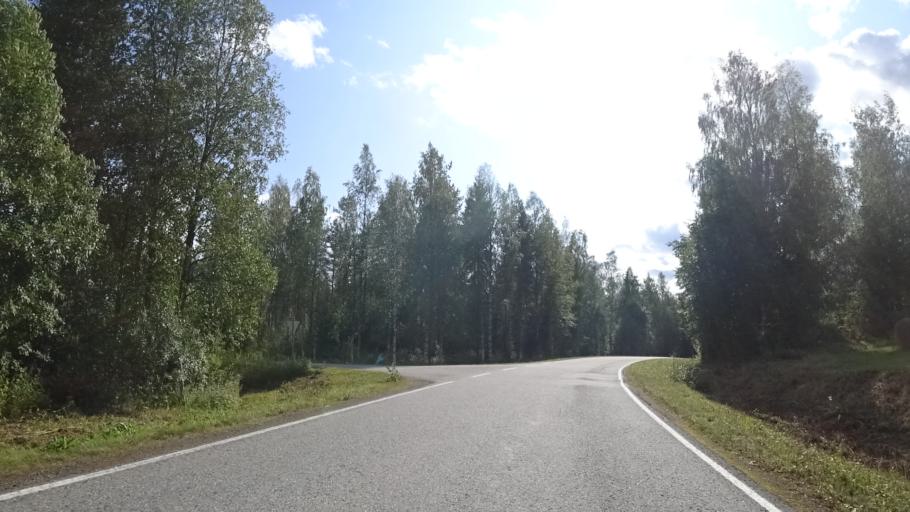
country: RU
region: Republic of Karelia
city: Vyartsilya
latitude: 62.2700
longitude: 30.8003
